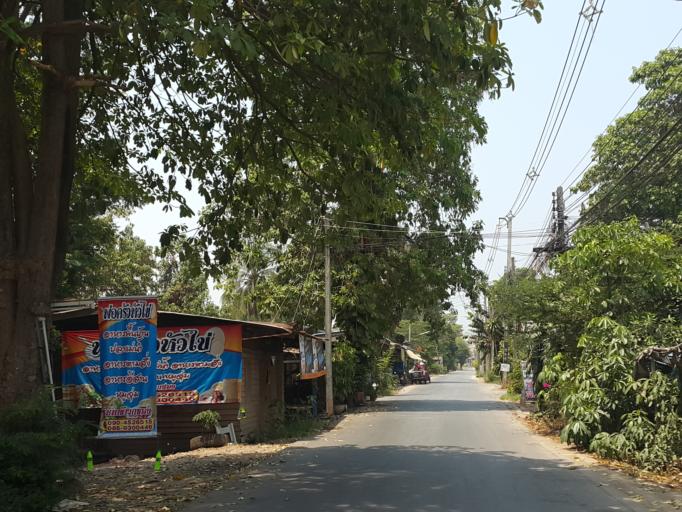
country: TH
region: Phitsanulok
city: Phitsanulok
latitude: 16.8135
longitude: 100.2591
